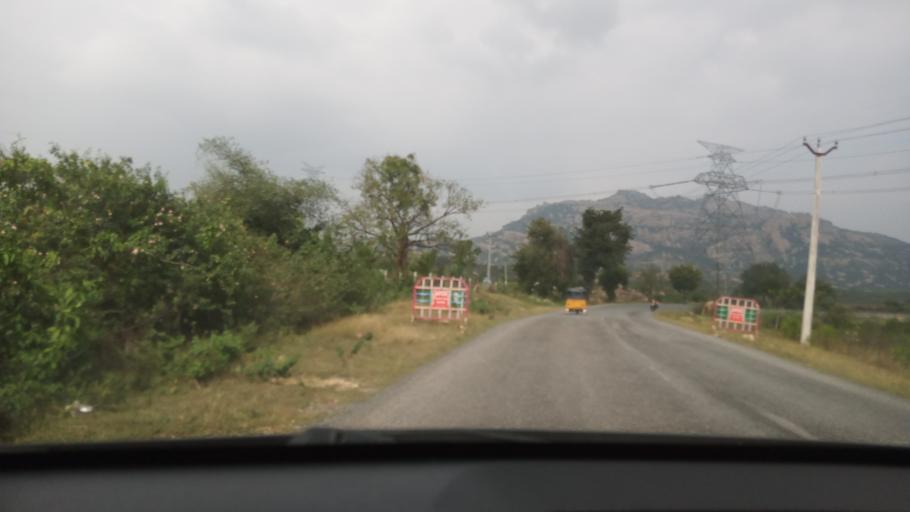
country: IN
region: Andhra Pradesh
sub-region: Chittoor
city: Madanapalle
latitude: 13.6557
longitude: 78.8358
